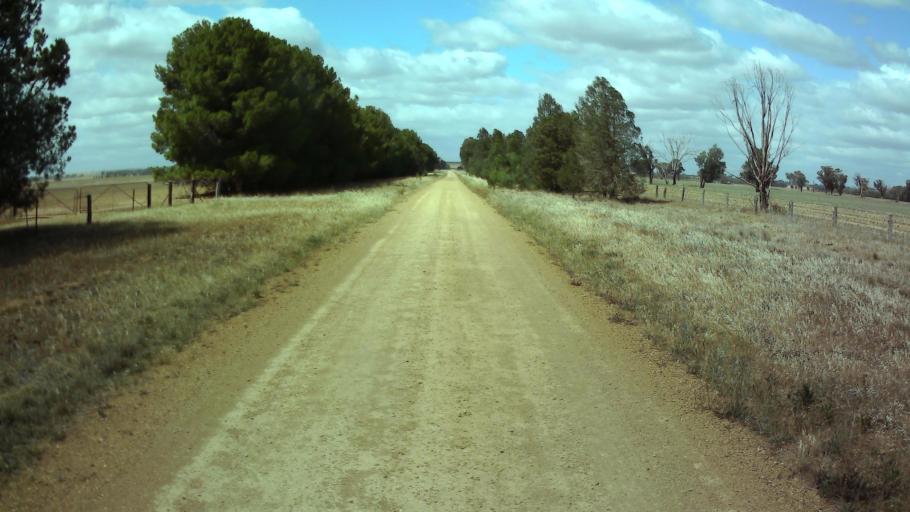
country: AU
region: New South Wales
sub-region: Weddin
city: Grenfell
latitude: -34.0469
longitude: 148.3328
